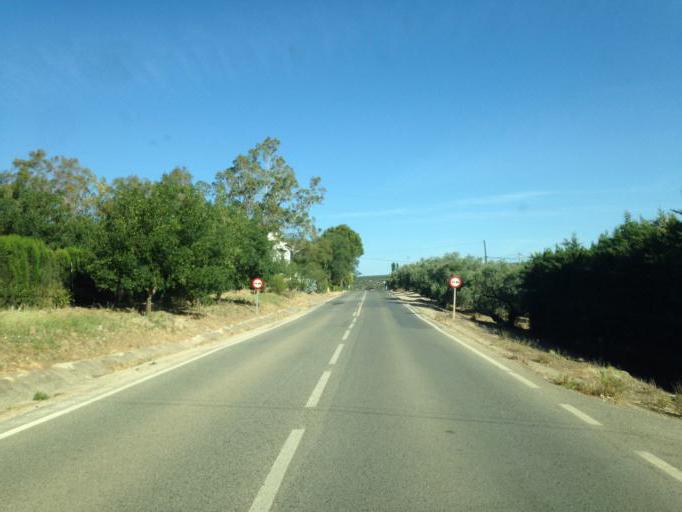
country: ES
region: Andalusia
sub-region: Provincia de Malaga
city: Villanueva del Rosario
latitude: 36.9936
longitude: -4.3713
